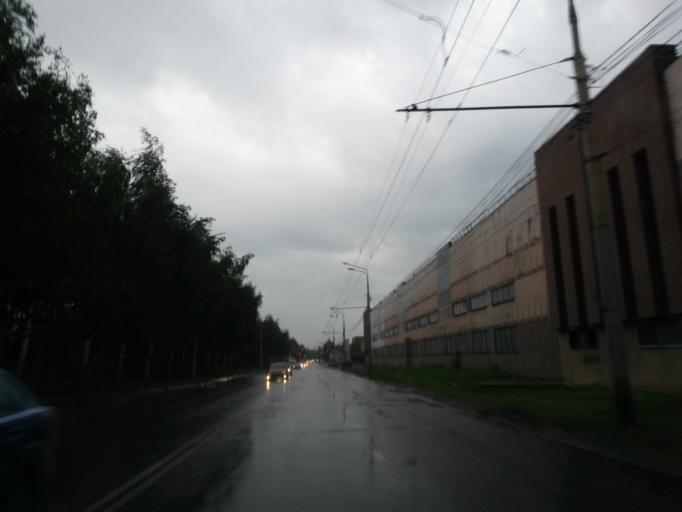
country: RU
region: Jaroslavl
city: Yaroslavl
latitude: 57.6573
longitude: 39.8657
